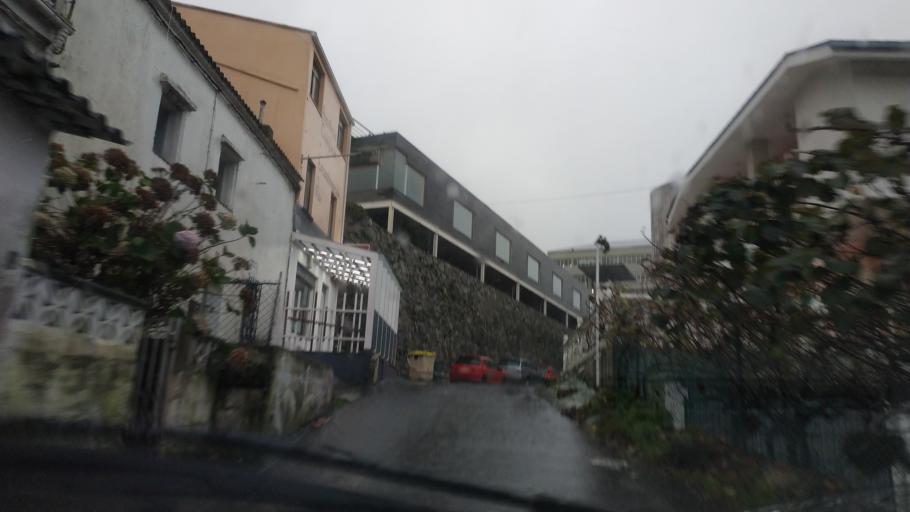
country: ES
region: Galicia
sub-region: Provincia da Coruna
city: A Coruna
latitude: 43.3289
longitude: -8.4086
